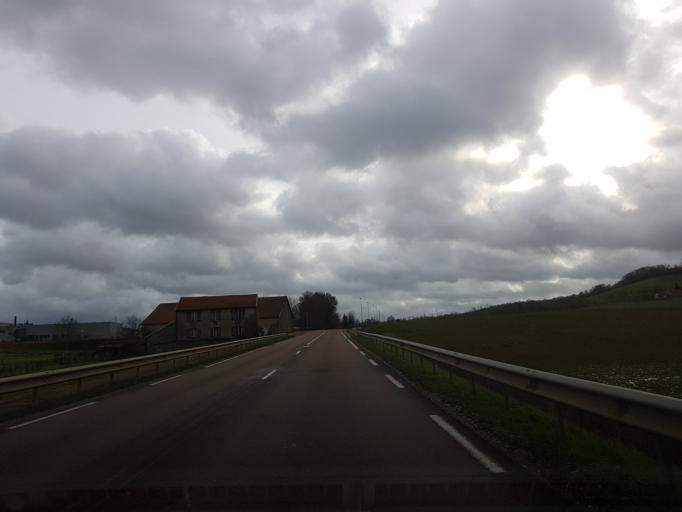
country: FR
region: Champagne-Ardenne
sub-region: Departement de la Haute-Marne
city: Langres
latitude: 47.8606
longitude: 5.3437
